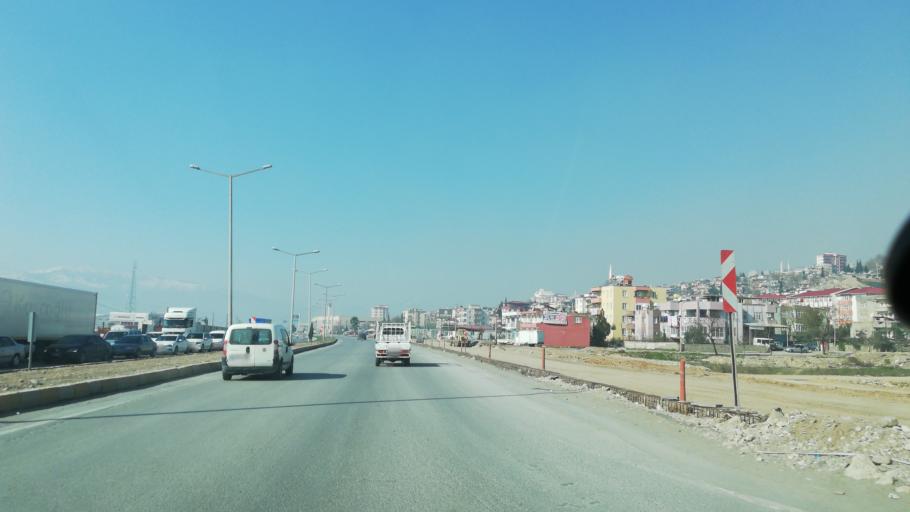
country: TR
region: Kahramanmaras
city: Kahramanmaras
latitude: 37.5694
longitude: 36.9167
